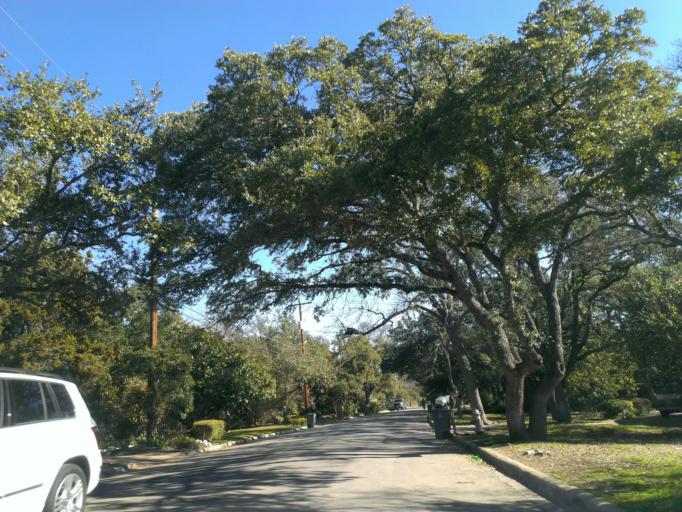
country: US
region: Texas
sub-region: Travis County
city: West Lake Hills
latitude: 30.3311
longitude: -97.7685
